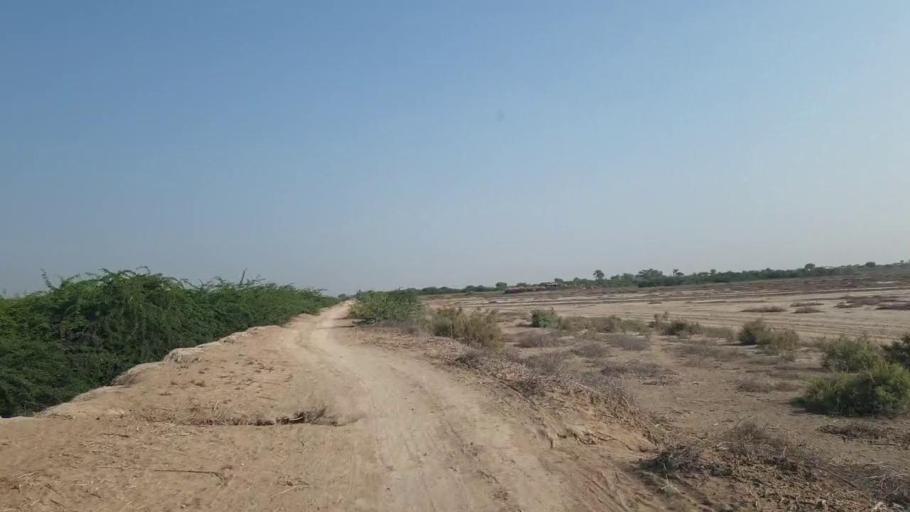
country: PK
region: Sindh
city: Badin
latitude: 24.4605
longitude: 68.7367
